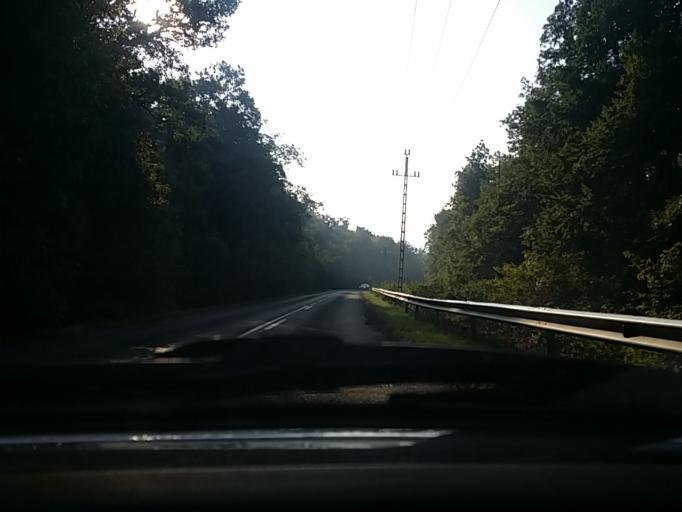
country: HU
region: Pest
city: Nagykovacsi
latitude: 47.7068
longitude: 19.0158
